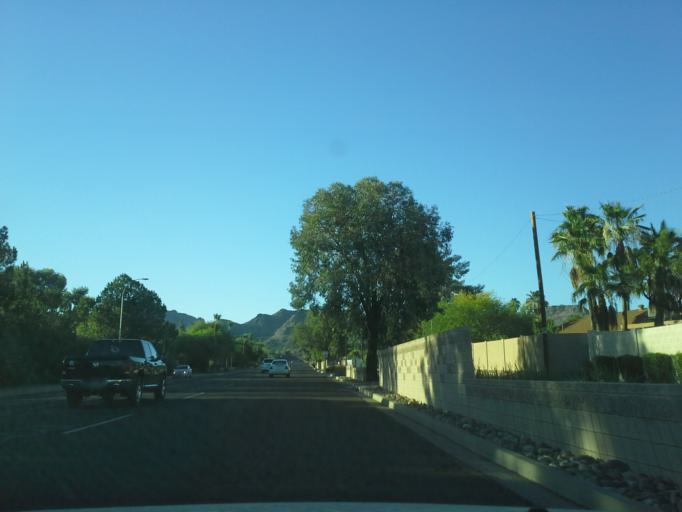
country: US
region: Arizona
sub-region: Maricopa County
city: Paradise Valley
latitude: 33.5149
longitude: -112.0129
